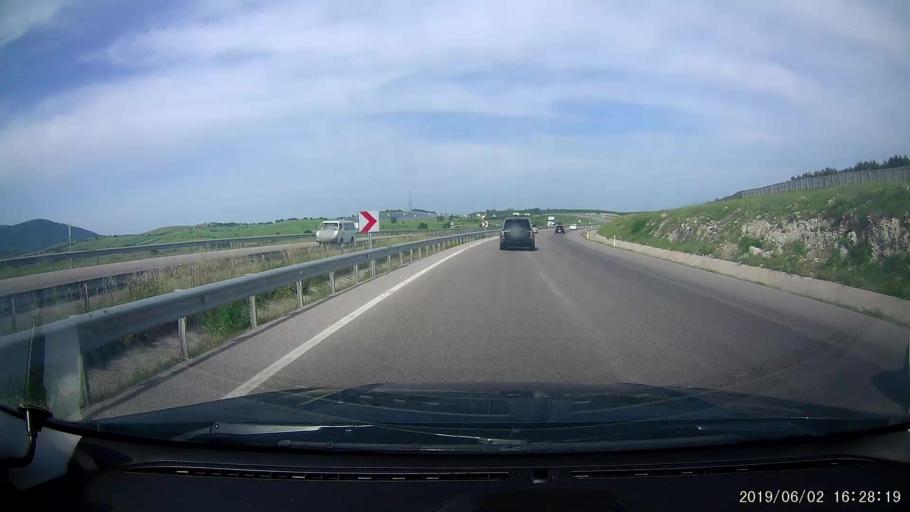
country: TR
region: Samsun
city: Ladik
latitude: 41.0070
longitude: 35.8445
